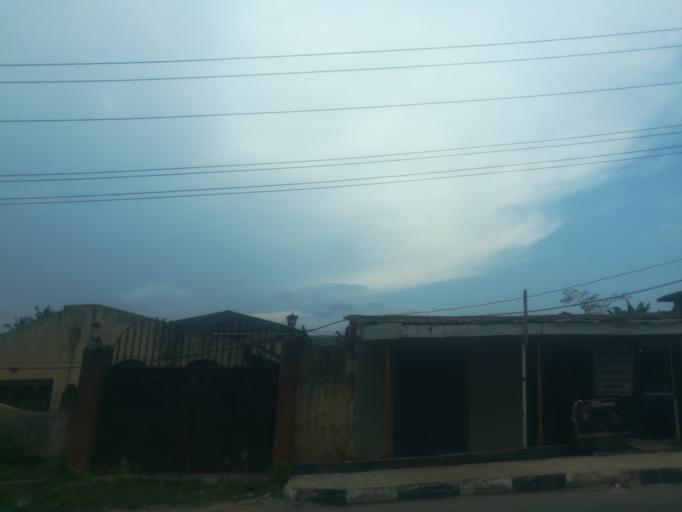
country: NG
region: Oyo
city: Ibadan
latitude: 7.3801
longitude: 3.8288
